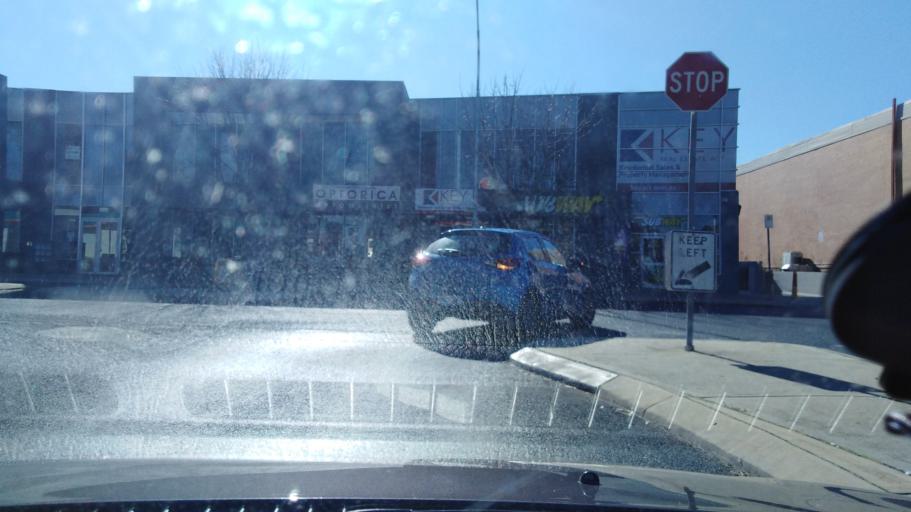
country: AU
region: Australian Capital Territory
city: Forrest
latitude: -35.3400
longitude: 149.0523
